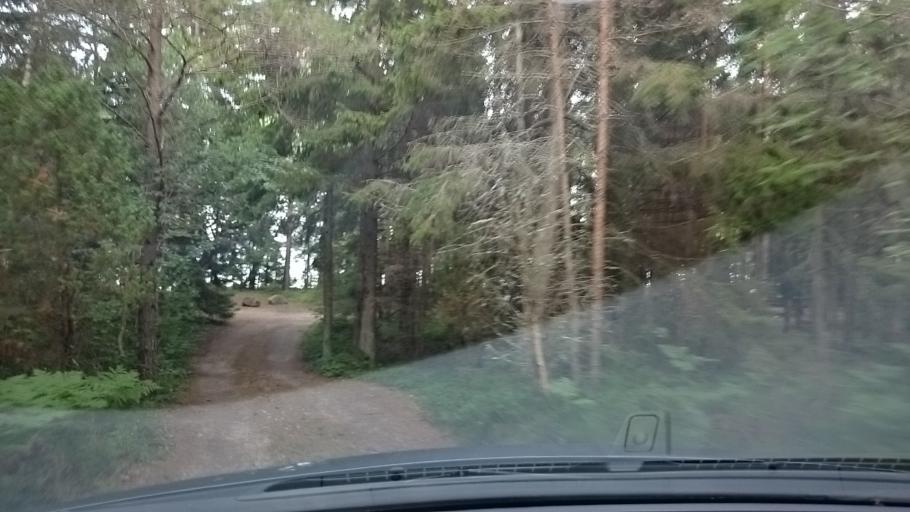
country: EE
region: Saare
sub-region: Kuressaare linn
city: Kuressaare
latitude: 58.4229
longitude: 22.0747
